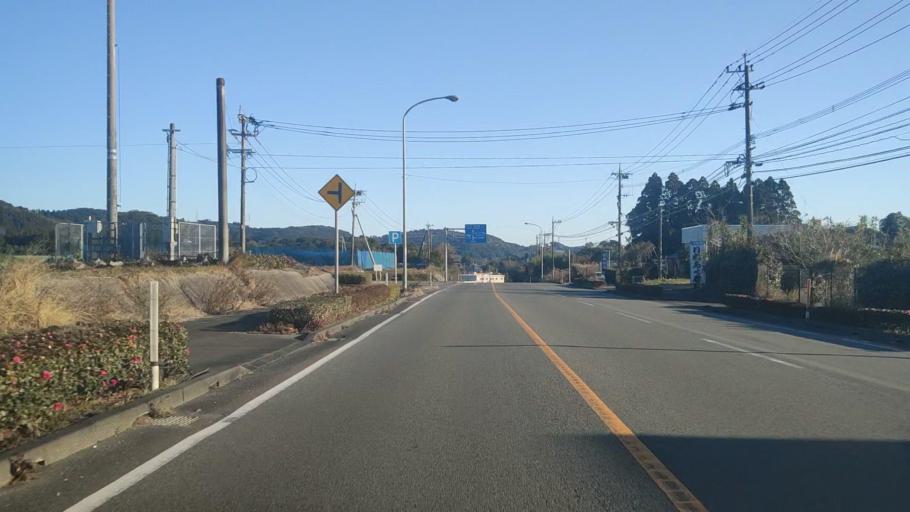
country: JP
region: Miyazaki
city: Takanabe
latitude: 32.3264
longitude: 131.6002
